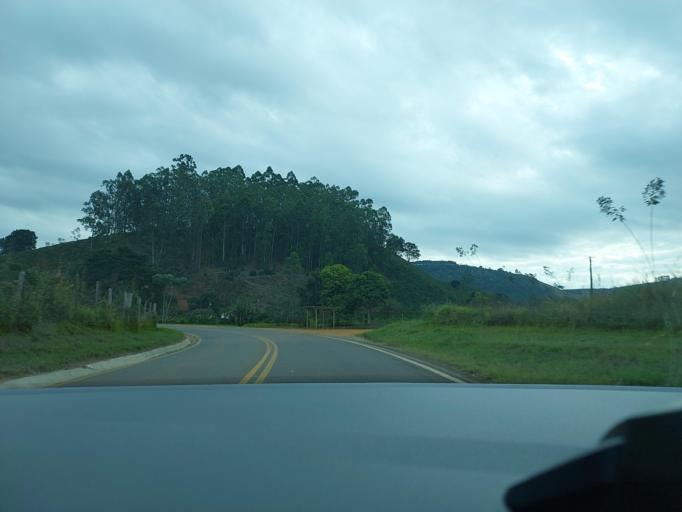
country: BR
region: Minas Gerais
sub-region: Mirai
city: Mirai
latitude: -21.0037
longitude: -42.5526
